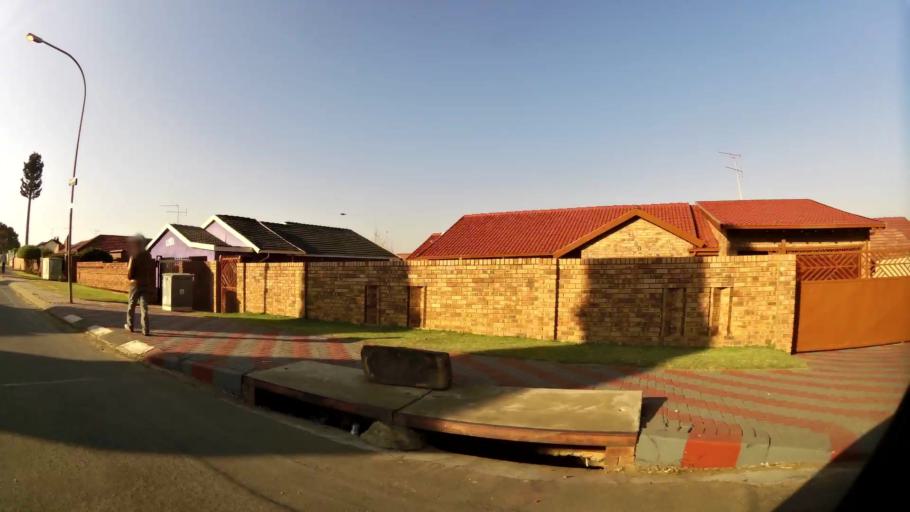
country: ZA
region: Gauteng
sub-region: City of Johannesburg Metropolitan Municipality
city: Soweto
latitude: -26.2540
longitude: 27.9535
